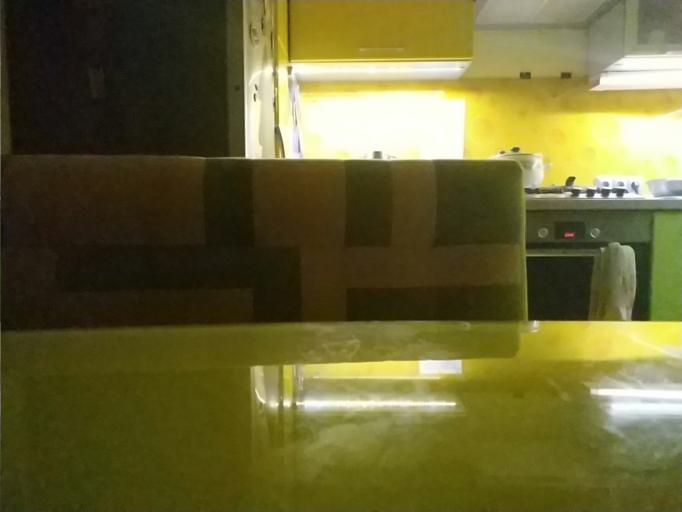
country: RU
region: Republic of Karelia
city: Pyaozerskiy
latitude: 65.7723
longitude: 30.4856
